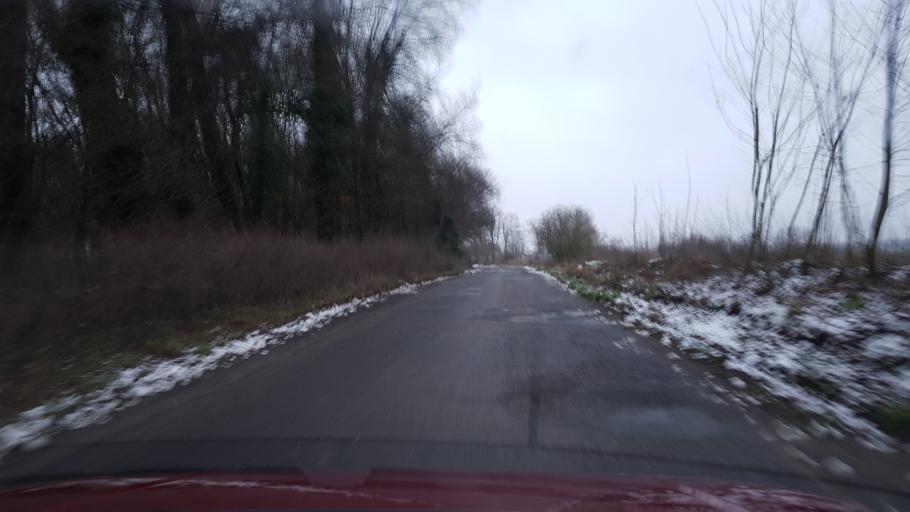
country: PL
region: West Pomeranian Voivodeship
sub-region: Powiat goleniowski
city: Mosty
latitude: 53.5011
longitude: 14.9419
